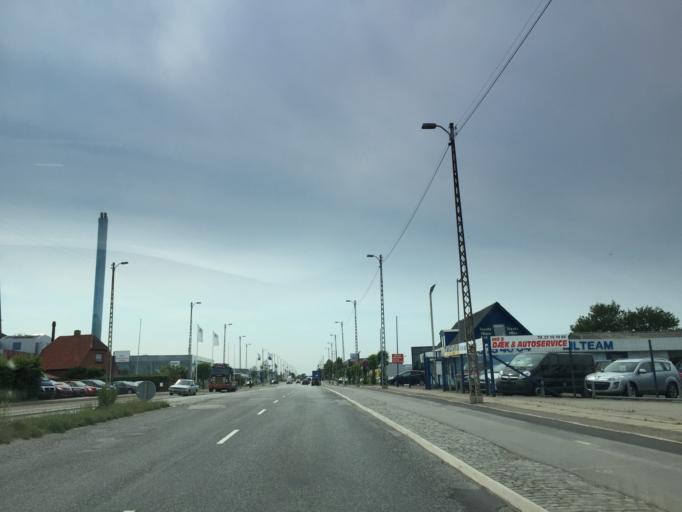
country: DK
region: Zealand
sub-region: Roskilde Kommune
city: Vindinge
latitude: 55.6435
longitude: 12.1272
